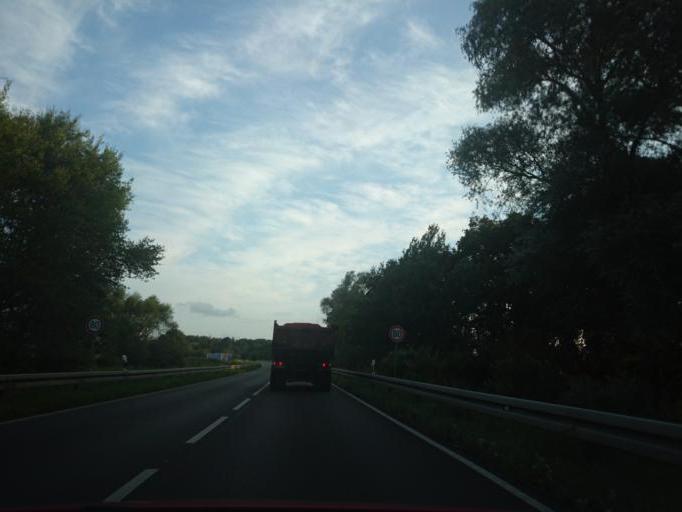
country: DE
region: Mecklenburg-Vorpommern
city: Mesekenhagen
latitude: 54.1612
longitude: 13.3086
